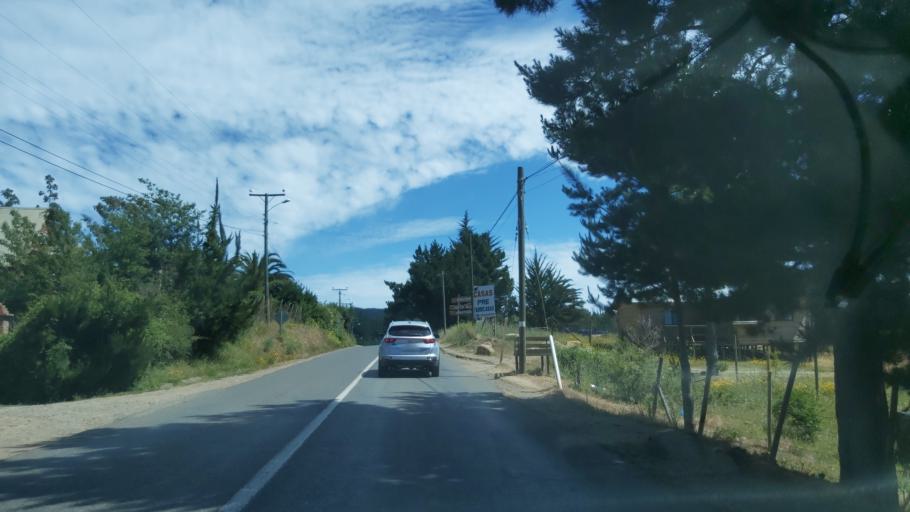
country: CL
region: Maule
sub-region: Provincia de Talca
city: Constitucion
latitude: -35.5050
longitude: -72.5201
